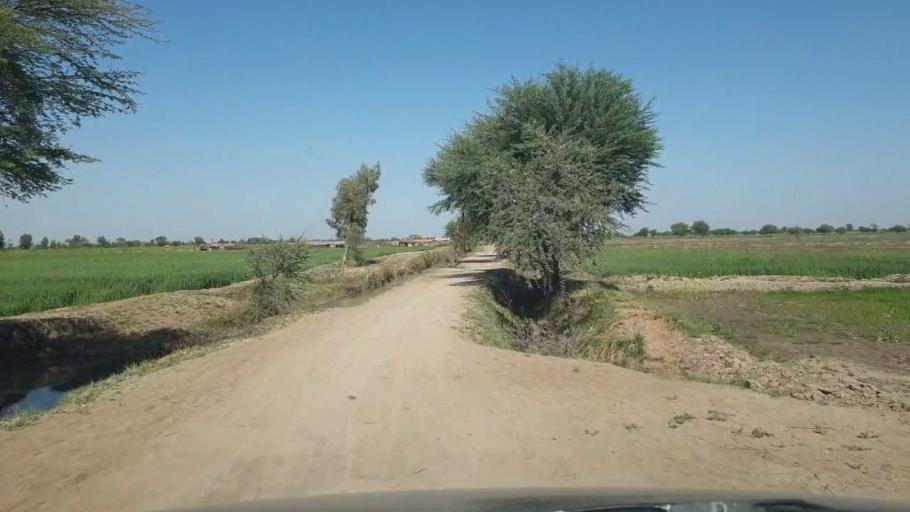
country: PK
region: Sindh
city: Dhoro Naro
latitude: 25.3808
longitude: 69.6016
